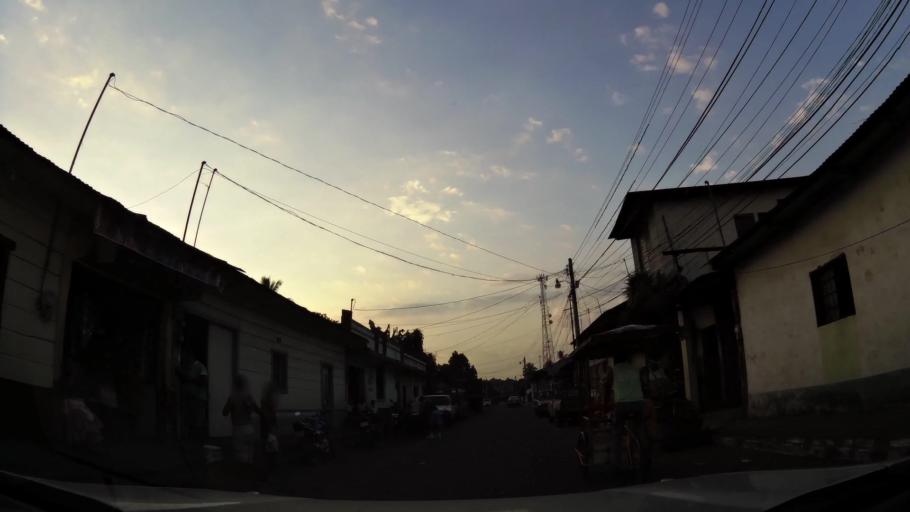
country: GT
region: Retalhuleu
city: San Sebastian
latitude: 14.5639
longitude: -91.6499
